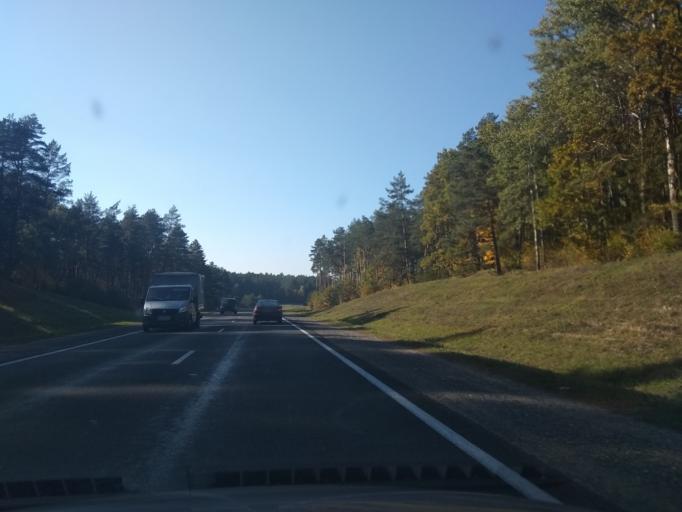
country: BY
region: Grodnenskaya
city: Slonim
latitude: 53.0529
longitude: 25.3288
